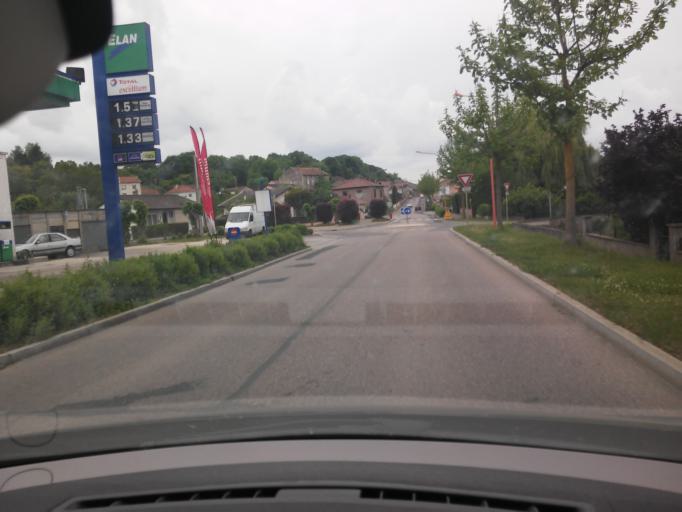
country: FR
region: Lorraine
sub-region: Departement de la Meuse
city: Lerouville
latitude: 48.7886
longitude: 5.5524
